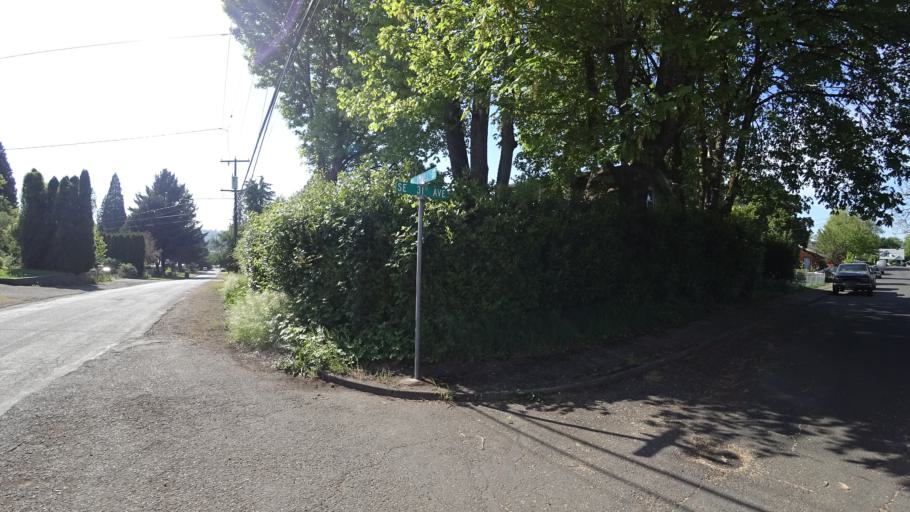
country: US
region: Oregon
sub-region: Clackamas County
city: Milwaukie
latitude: 45.4588
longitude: -122.6309
